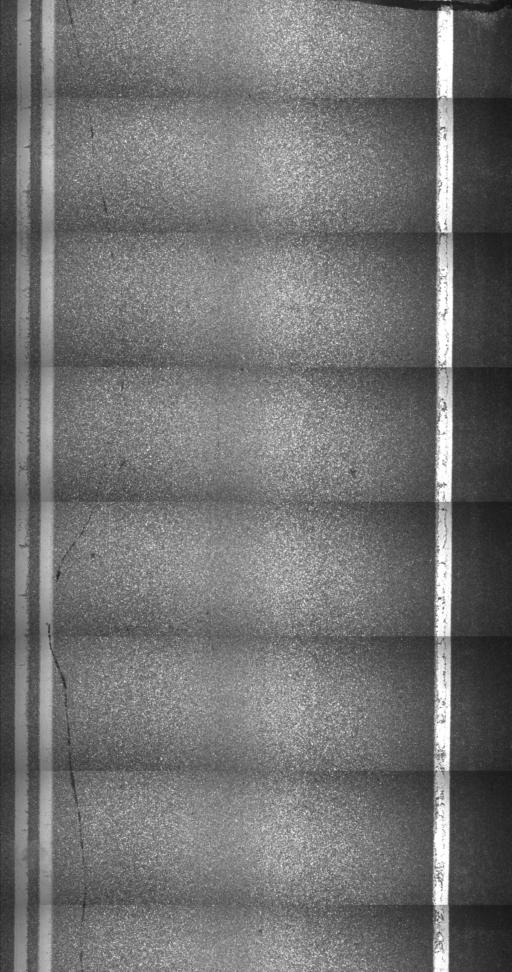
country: US
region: Vermont
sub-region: Washington County
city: Northfield
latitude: 44.0974
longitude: -72.8621
